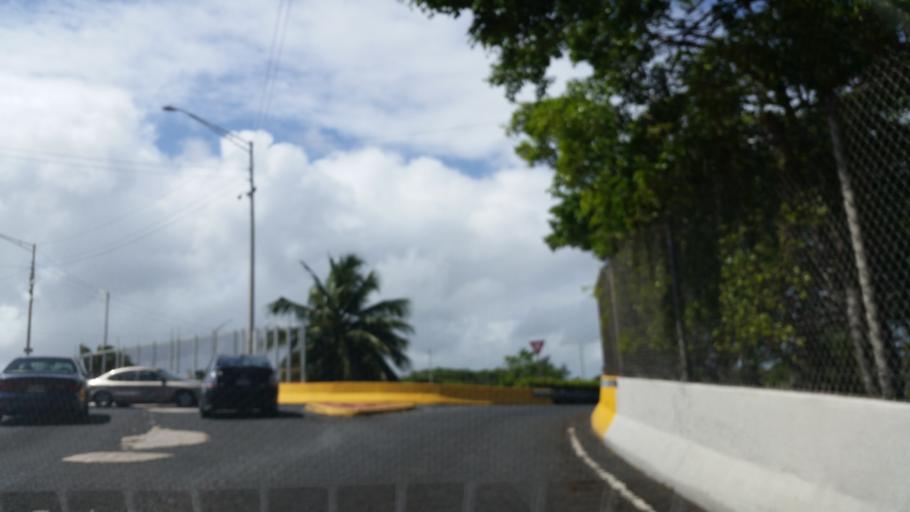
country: PR
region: San Juan
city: San Juan
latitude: 18.4462
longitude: -66.0346
